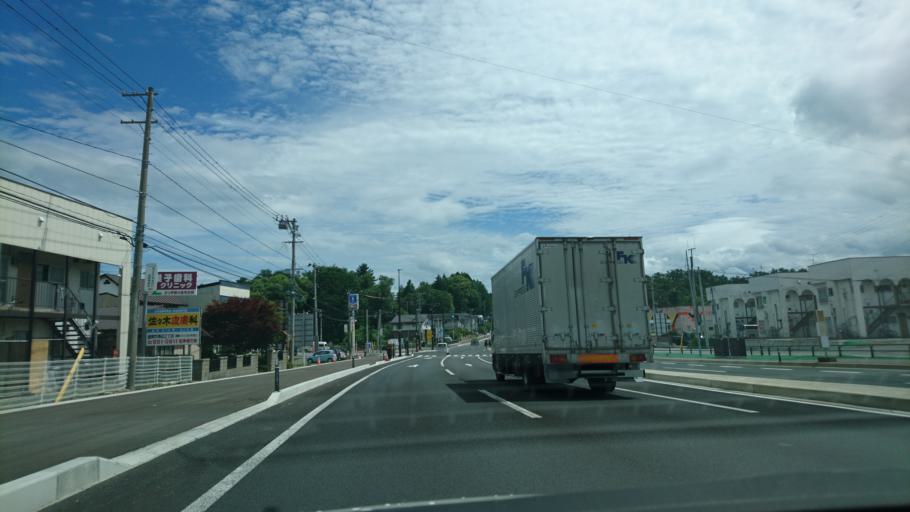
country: JP
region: Iwate
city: Morioka-shi
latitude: 39.7704
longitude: 141.1305
